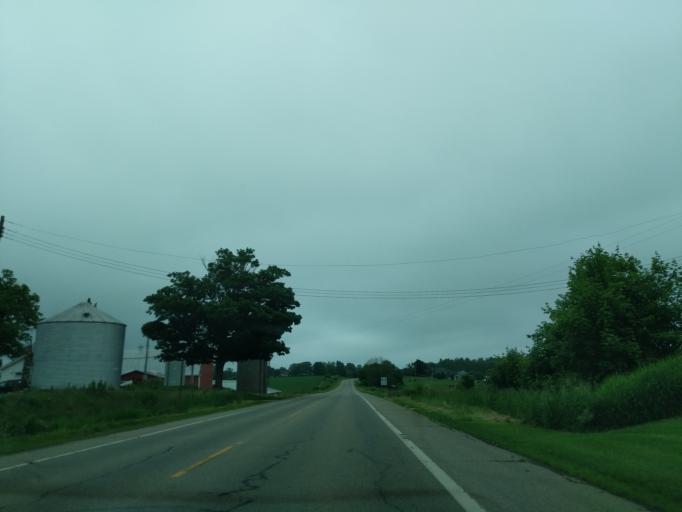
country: US
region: Michigan
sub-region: Hillsdale County
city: Litchfield
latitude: 42.0290
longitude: -84.7191
